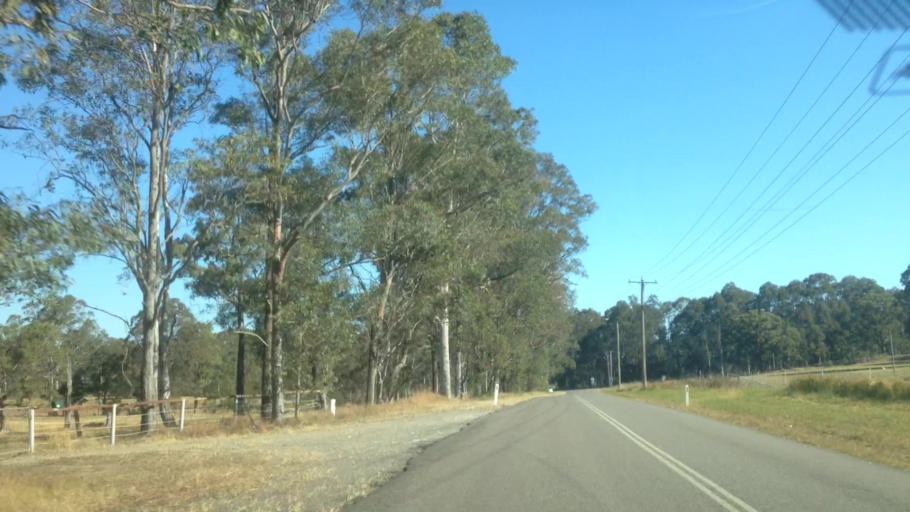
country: AU
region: New South Wales
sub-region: Lake Macquarie Shire
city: Cooranbong
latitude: -33.1142
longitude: 151.4477
